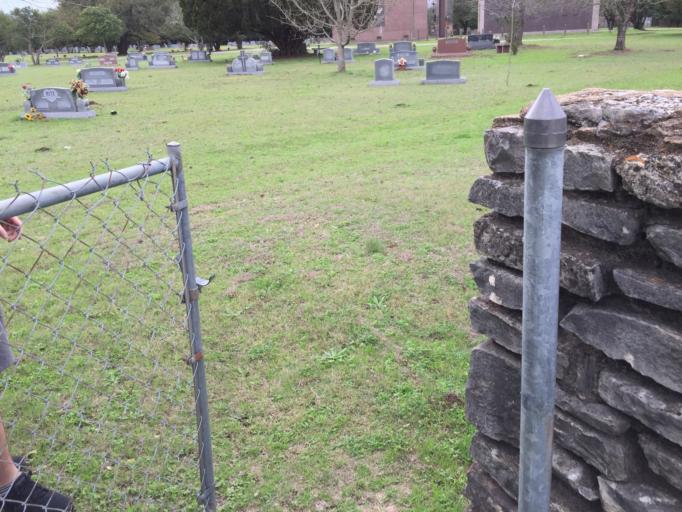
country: US
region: Texas
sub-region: Travis County
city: Manchaca
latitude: 30.1439
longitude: -97.8219
